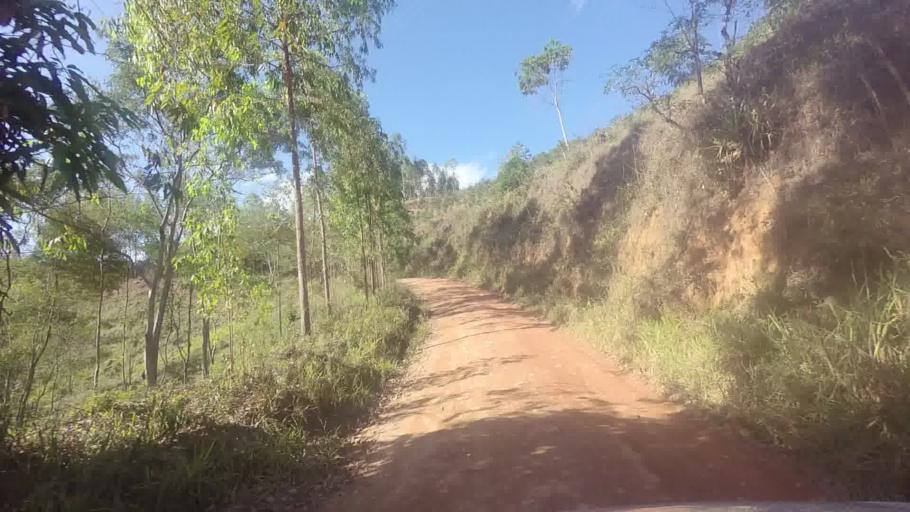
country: BR
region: Espirito Santo
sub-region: Sao Jose Do Calcado
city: Sao Jose do Calcado
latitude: -21.0269
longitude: -41.5779
